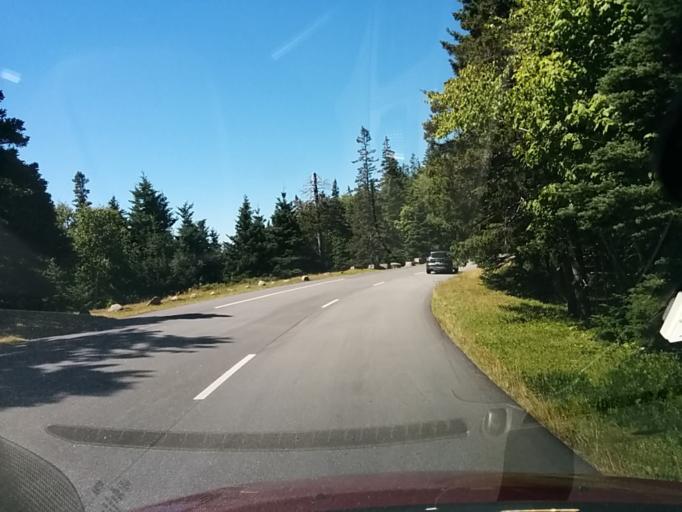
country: US
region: Maine
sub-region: Hancock County
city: Bar Harbor
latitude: 44.2987
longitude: -68.2086
